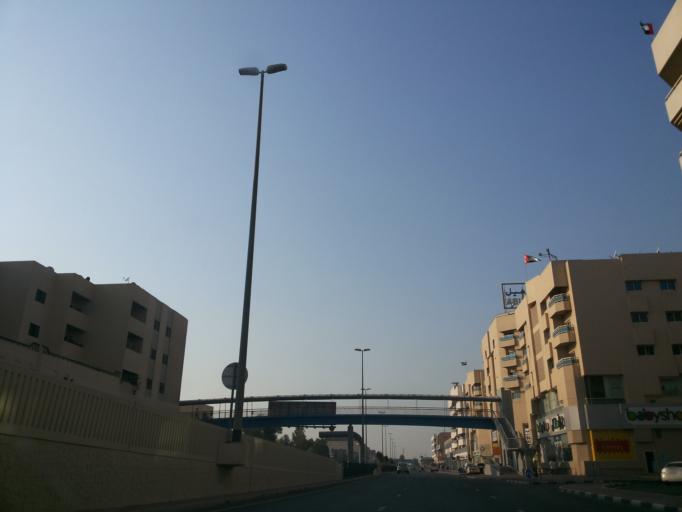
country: AE
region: Ash Shariqah
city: Sharjah
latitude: 25.2774
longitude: 55.3468
